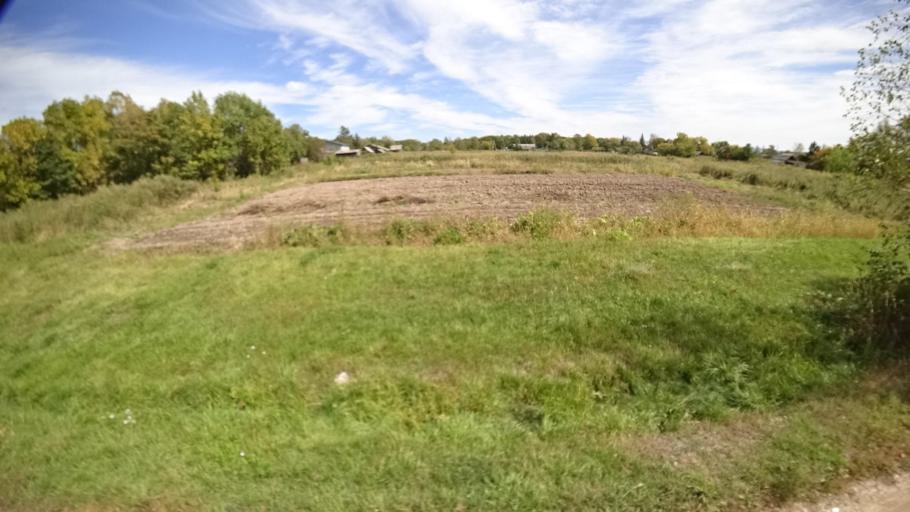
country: RU
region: Primorskiy
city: Yakovlevka
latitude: 44.6473
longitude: 133.5880
